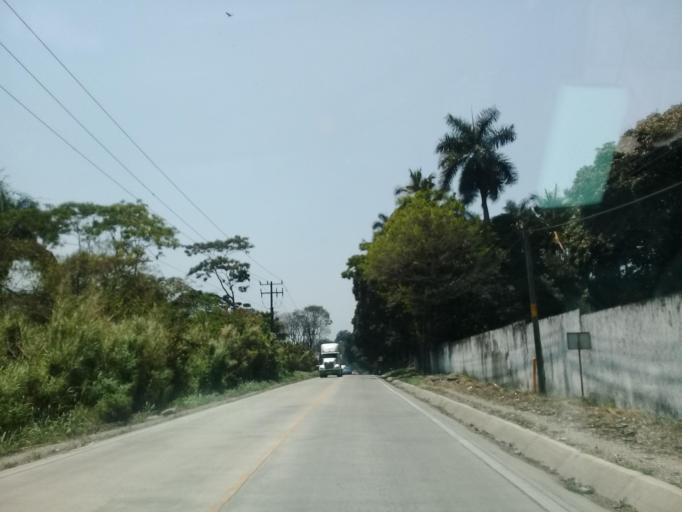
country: MX
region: Veracruz
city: Paraje Nuevo
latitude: 18.8725
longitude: -96.8725
